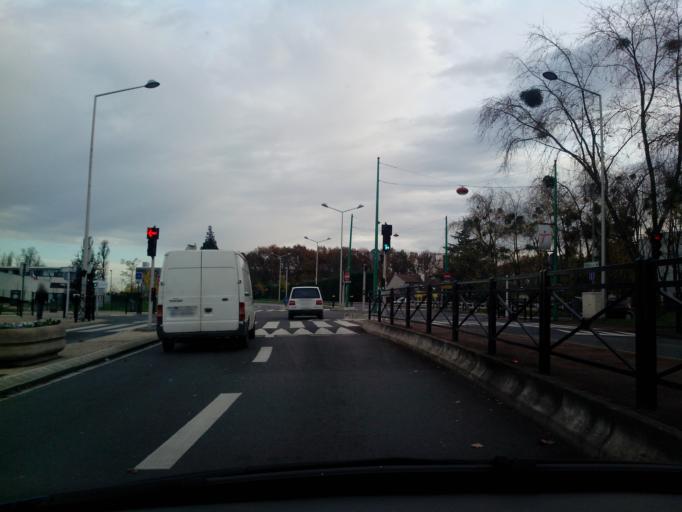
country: FR
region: Ile-de-France
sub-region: Departement de l'Essonne
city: Evry
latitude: 48.6235
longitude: 2.4535
